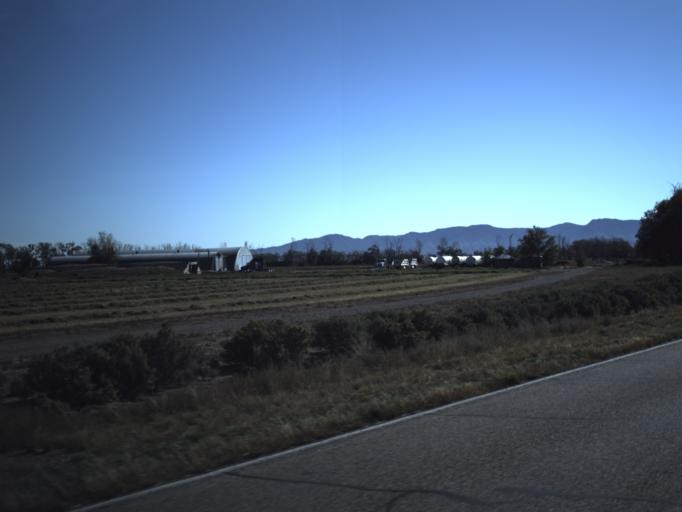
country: US
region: Utah
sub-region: Washington County
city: Enterprise
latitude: 37.7149
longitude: -113.6714
